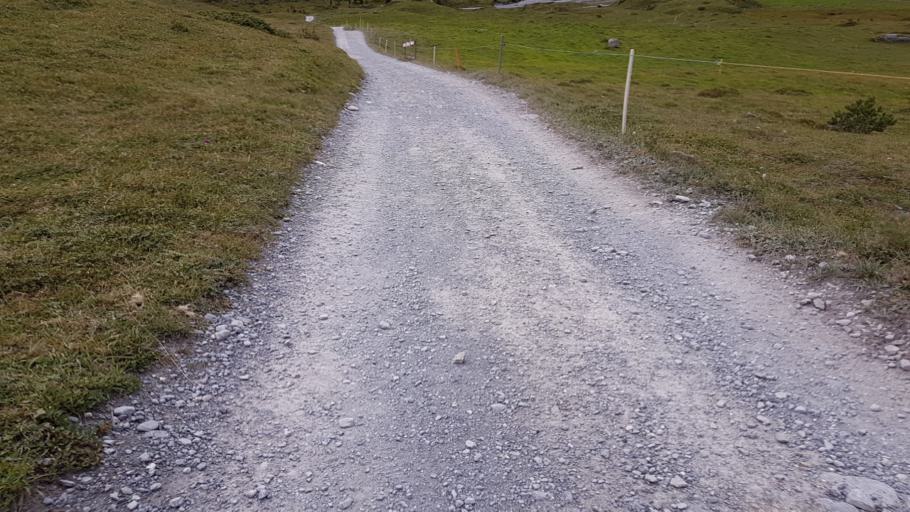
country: CH
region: Bern
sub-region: Frutigen-Niedersimmental District
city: Kandersteg
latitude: 46.4488
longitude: 7.6432
